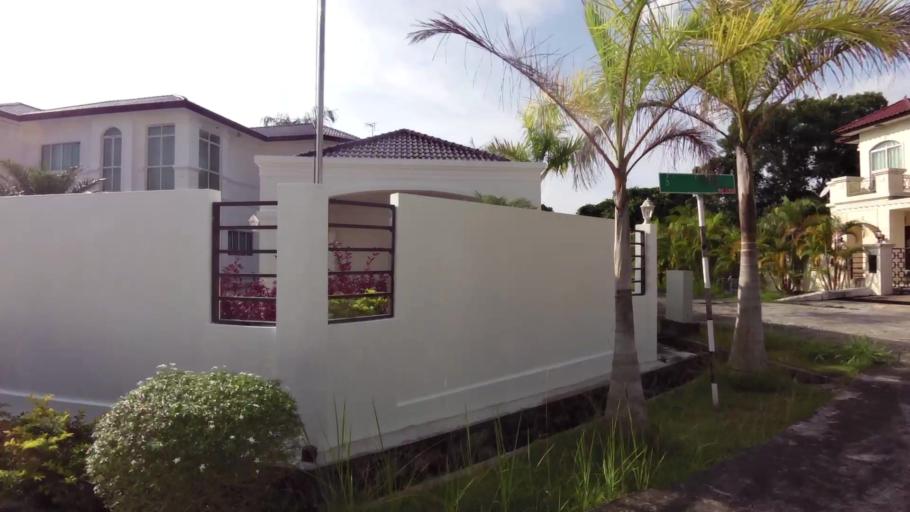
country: BN
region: Brunei and Muara
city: Bandar Seri Begawan
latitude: 4.9679
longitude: 114.9729
